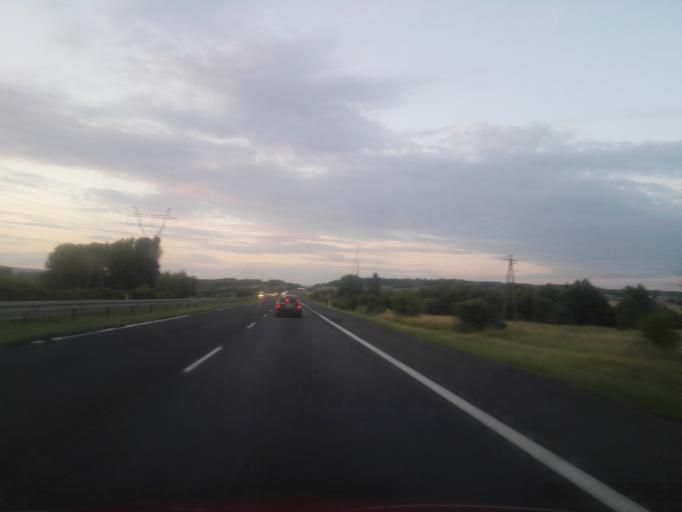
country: PL
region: Lodz Voivodeship
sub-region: Powiat radomszczanski
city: Radomsko
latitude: 51.1301
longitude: 19.4134
